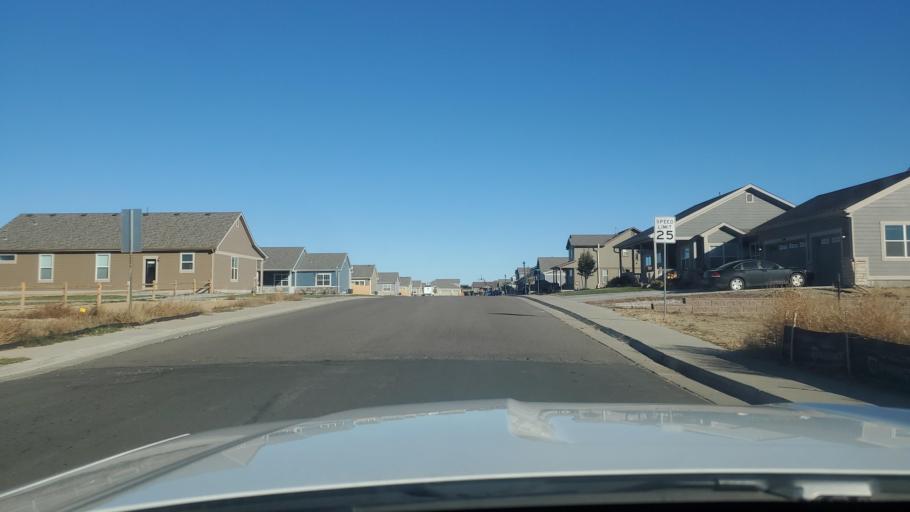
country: US
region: Colorado
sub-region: Adams County
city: Strasburg
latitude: 39.7476
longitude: -104.3261
